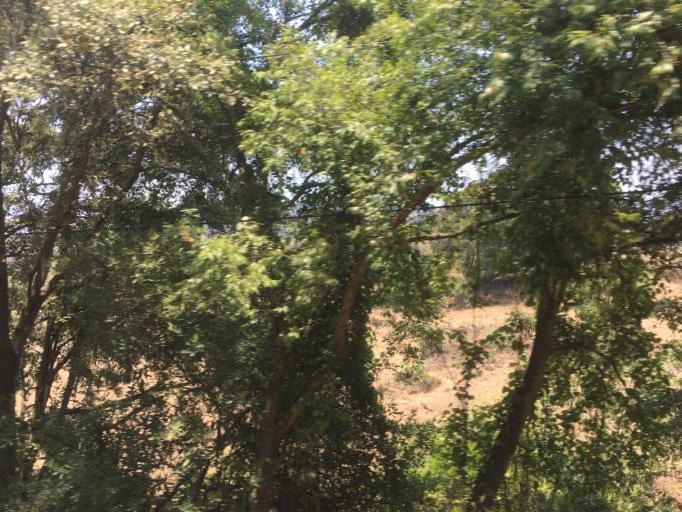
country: MX
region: Michoacan
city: Quiroga
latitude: 19.6616
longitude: -101.5126
